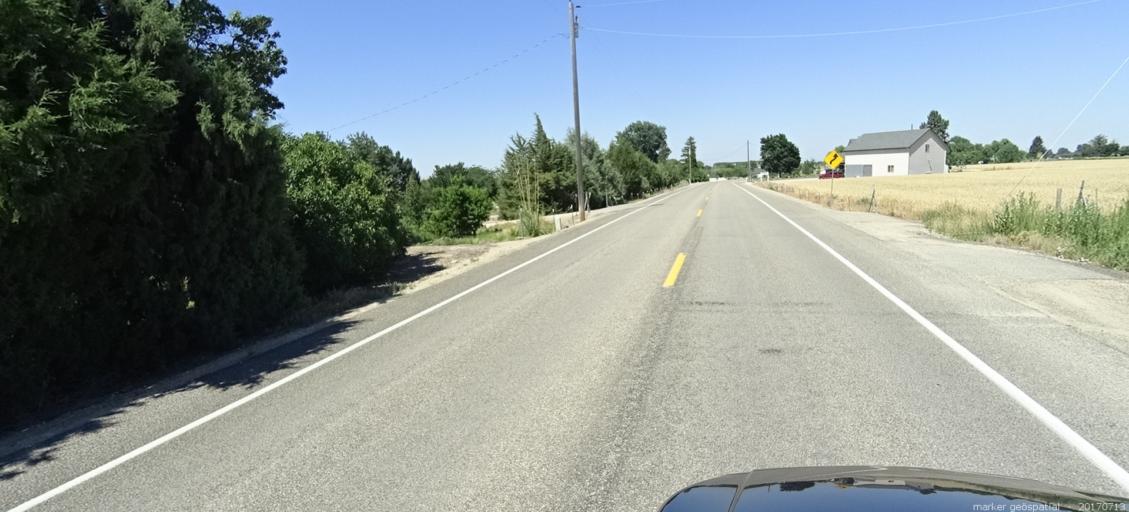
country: US
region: Idaho
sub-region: Ada County
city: Kuna
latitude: 43.5321
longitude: -116.4583
